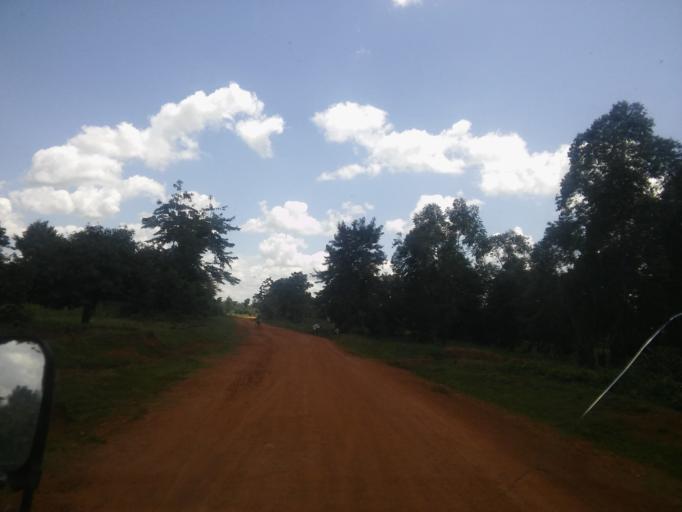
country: UG
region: Eastern Region
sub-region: Budaka District
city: Budaka
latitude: 1.1117
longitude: 33.9604
